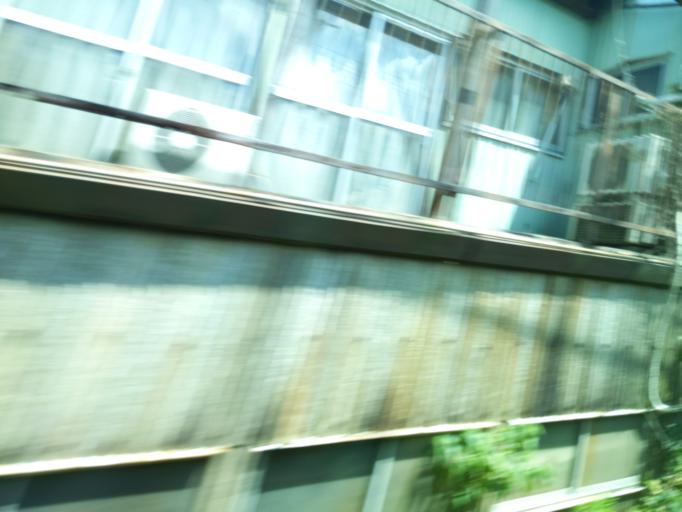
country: JP
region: Tokyo
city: Chofugaoka
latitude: 35.6284
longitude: 139.5571
